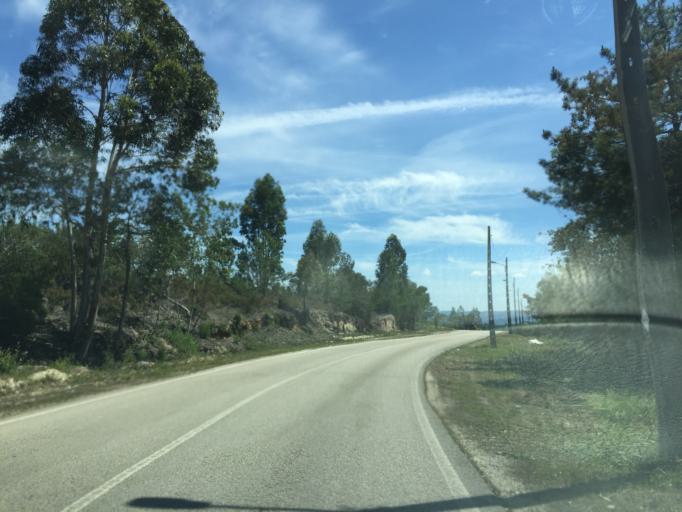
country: PT
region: Coimbra
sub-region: Soure
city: Soure
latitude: 40.0625
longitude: -8.6882
